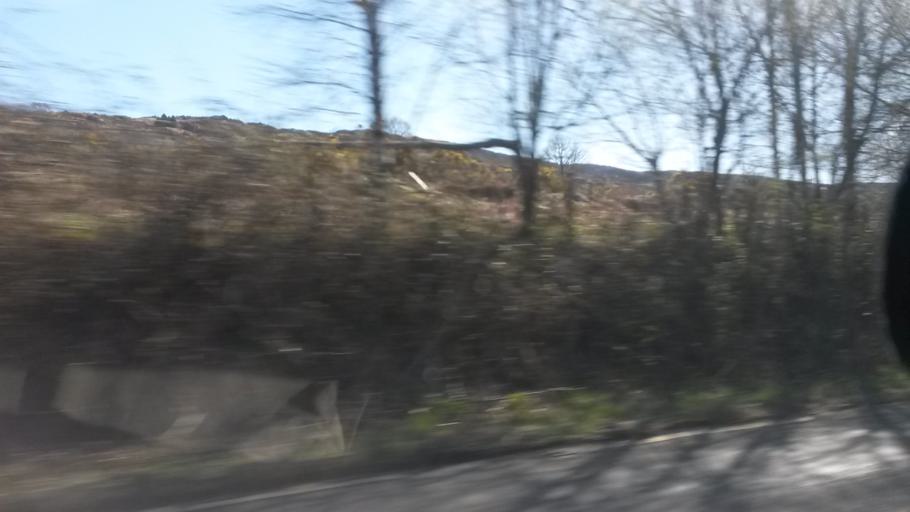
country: IE
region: Munster
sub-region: Ciarrai
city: Cill Airne
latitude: 51.9434
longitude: -9.3855
